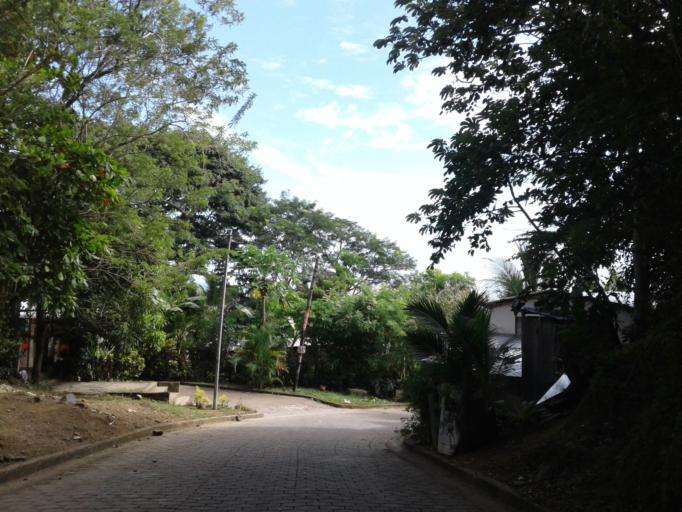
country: NI
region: Rivas
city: Cardenas
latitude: 11.2488
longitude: -85.6265
